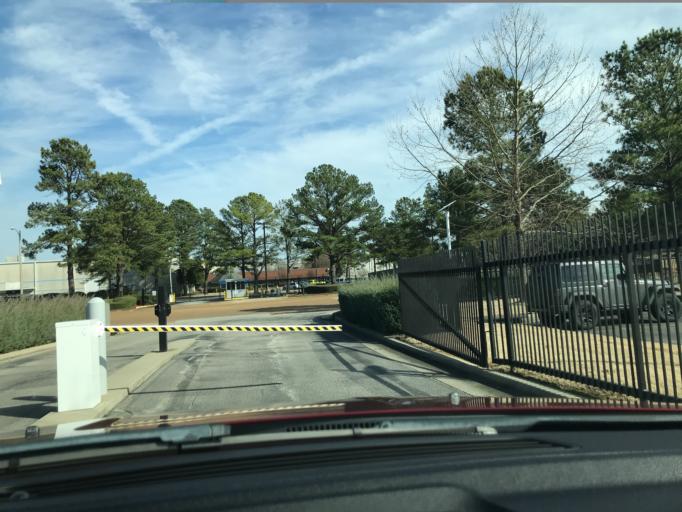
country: US
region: Tennessee
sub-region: Shelby County
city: Germantown
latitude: 35.0496
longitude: -89.7845
